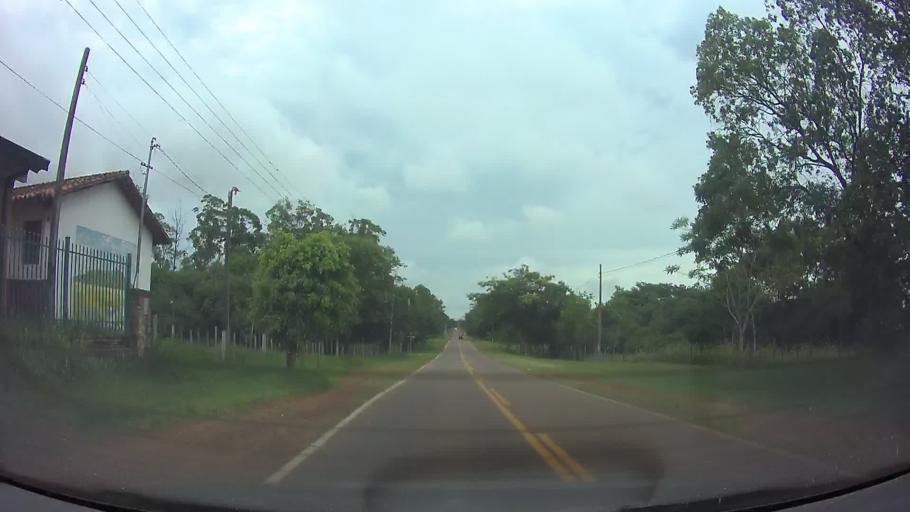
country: PY
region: Paraguari
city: Carapegua
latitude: -25.7889
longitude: -57.2145
